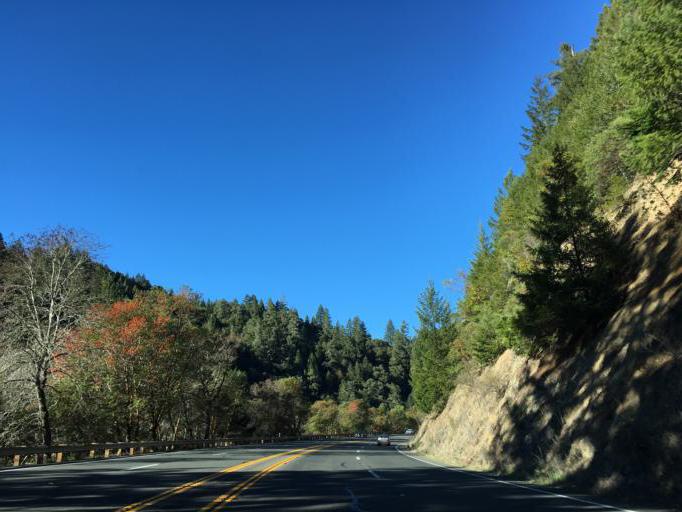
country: US
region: California
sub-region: Mendocino County
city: Brooktrails
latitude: 39.5300
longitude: -123.4040
